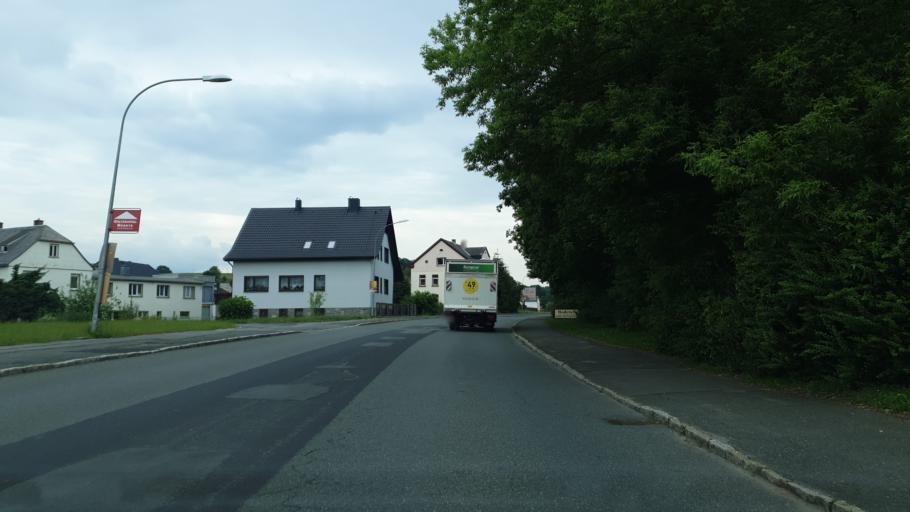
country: DE
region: Saxony
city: Rodewisch
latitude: 50.5393
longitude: 12.3985
